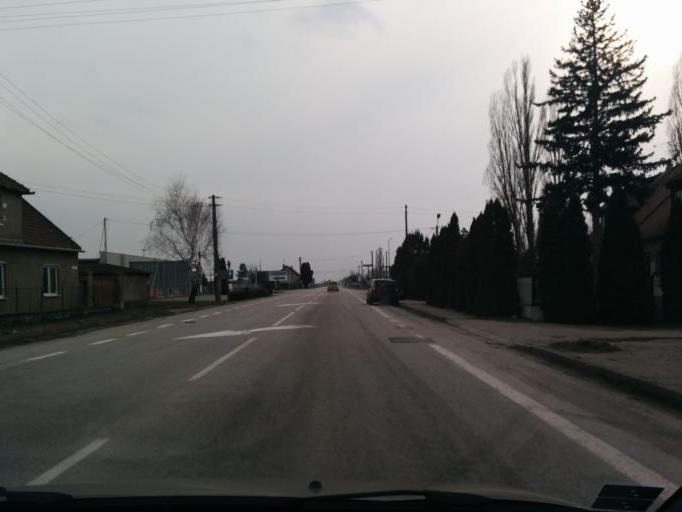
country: SK
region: Trnavsky
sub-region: Okres Galanta
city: Galanta
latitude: 48.2810
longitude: 17.7258
